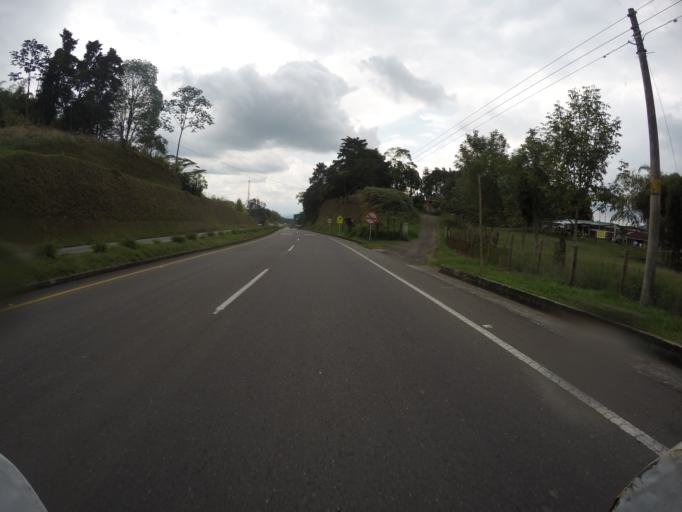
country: CO
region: Quindio
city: Filandia
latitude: 4.7417
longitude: -75.6609
